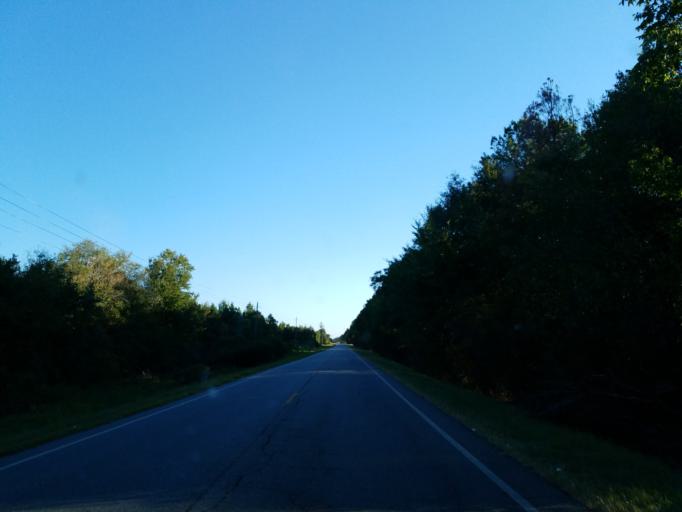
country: US
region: Georgia
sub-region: Worth County
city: Sylvester
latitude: 31.6373
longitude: -83.8657
